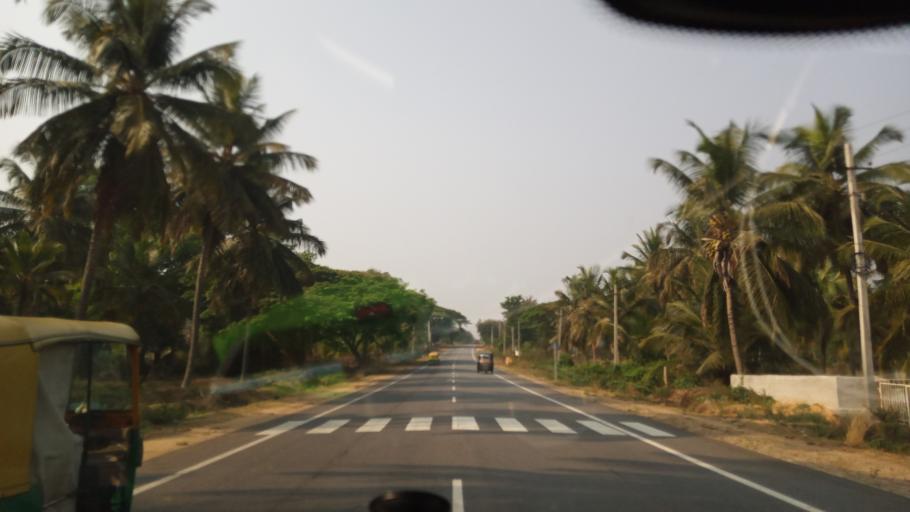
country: IN
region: Karnataka
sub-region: Mandya
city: Belluru
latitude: 12.9292
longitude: 76.7494
